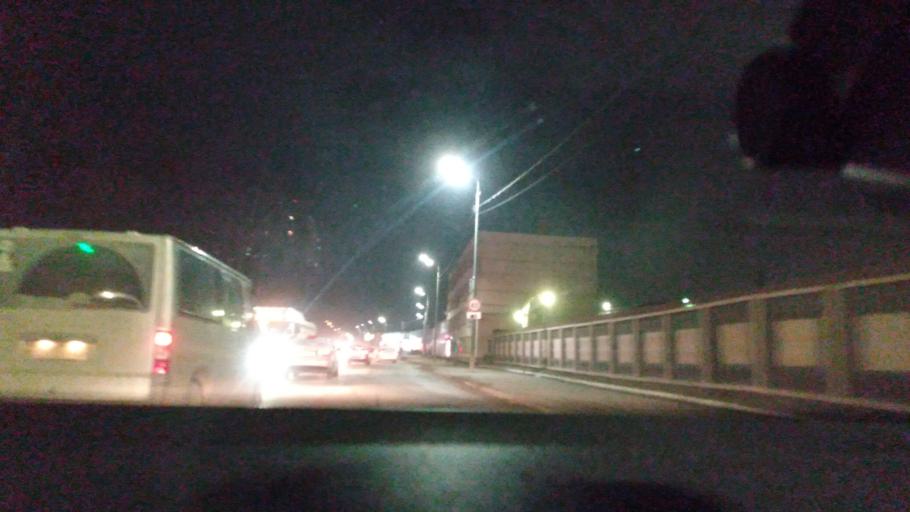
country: RU
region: Moskovskaya
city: Balashikha
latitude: 55.8199
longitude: 37.9531
